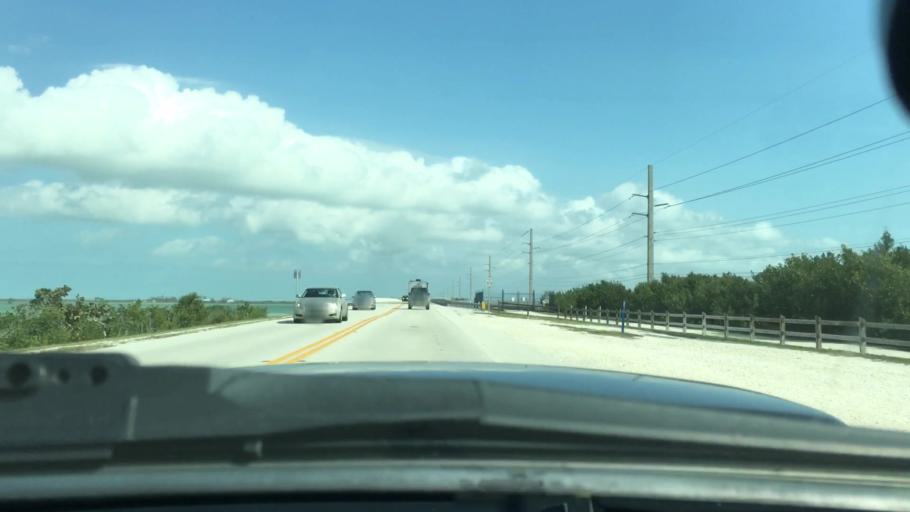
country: US
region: Florida
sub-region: Monroe County
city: Big Coppitt Key
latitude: 24.6313
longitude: -81.5895
